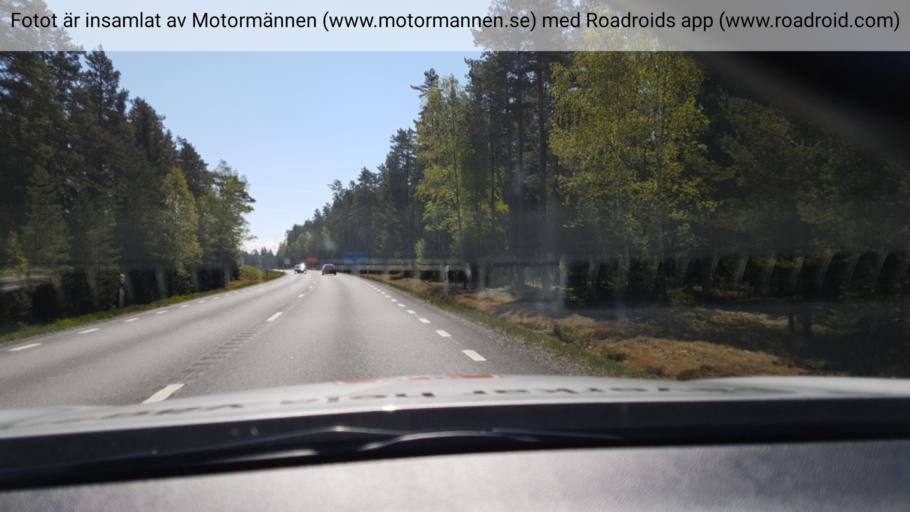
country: SE
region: Joenkoeping
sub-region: Mullsjo Kommun
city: Mullsjoe
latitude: 57.9087
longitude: 13.8589
